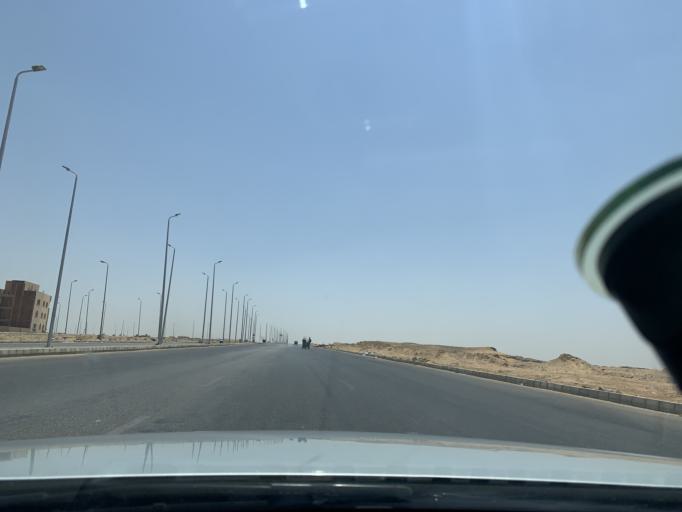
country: EG
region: Muhafazat al Qahirah
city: Halwan
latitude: 29.9942
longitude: 31.4687
